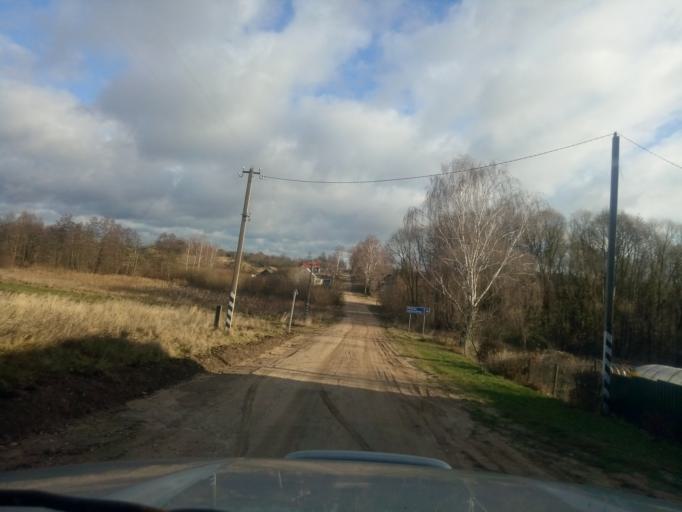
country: BY
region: Minsk
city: Tsimkavichy
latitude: 53.1478
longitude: 26.9756
